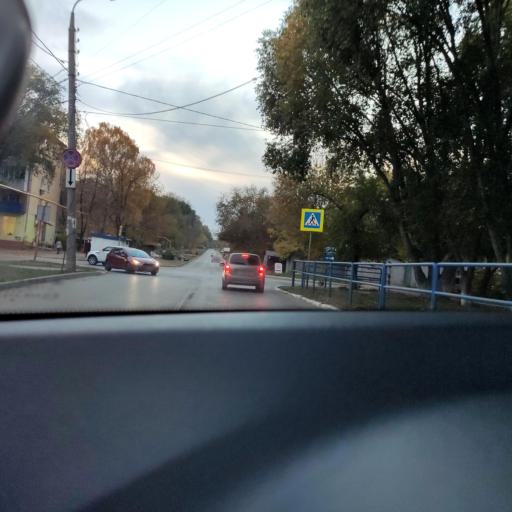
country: RU
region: Samara
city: Samara
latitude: 53.2233
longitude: 50.2285
